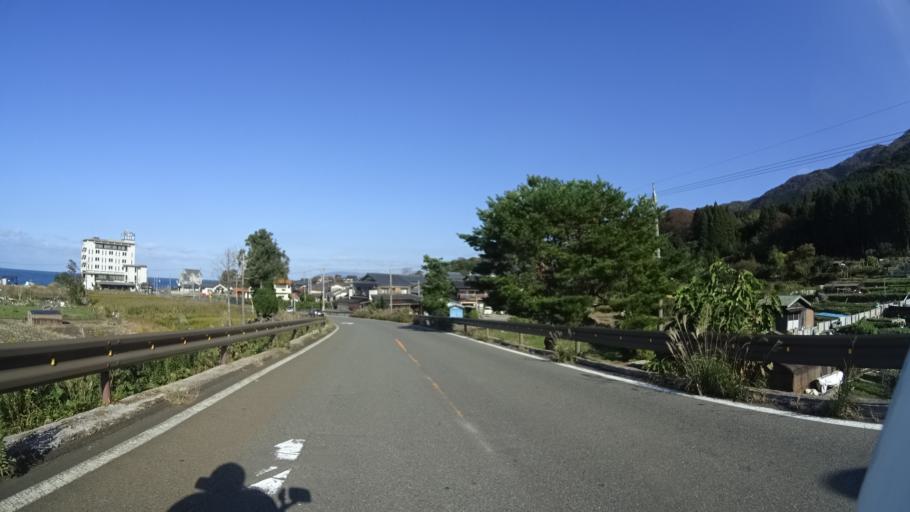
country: JP
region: Fukui
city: Tsuruga
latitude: 35.7457
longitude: 136.1025
